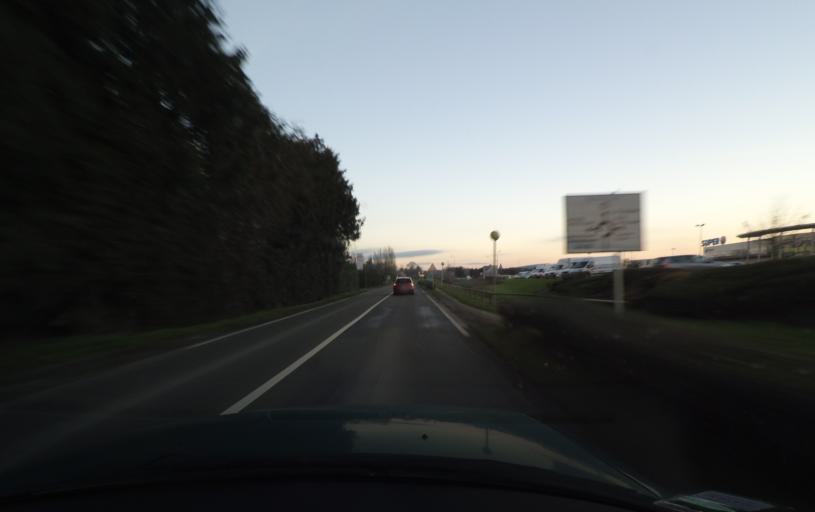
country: FR
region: Pays de la Loire
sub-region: Departement de la Mayenne
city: Evron
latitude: 48.1465
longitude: -0.4146
